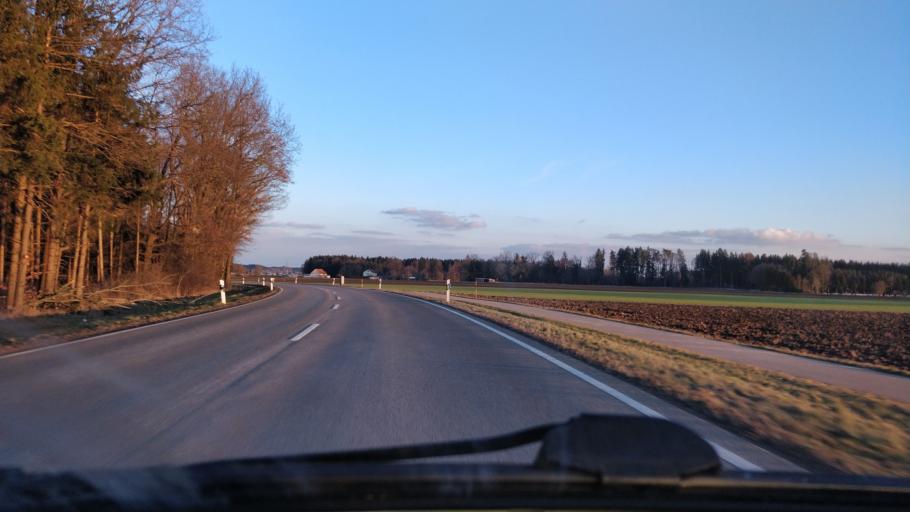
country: DE
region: Bavaria
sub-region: Swabia
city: Holzheim
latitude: 48.3696
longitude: 10.1242
